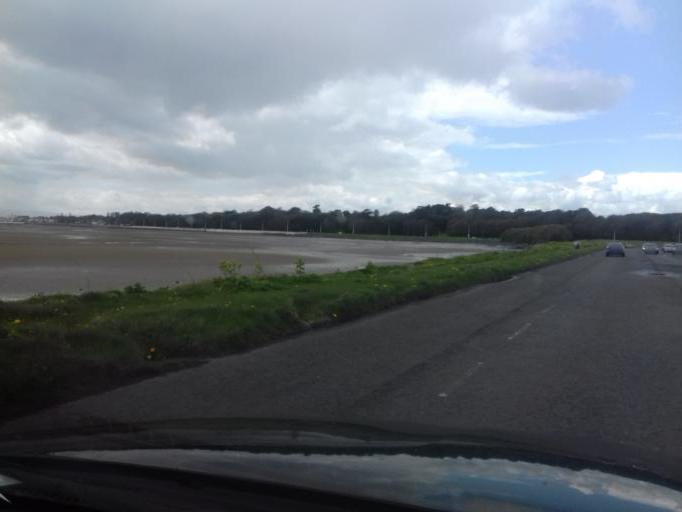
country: IE
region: Leinster
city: Dollymount
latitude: 53.3726
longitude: -6.1587
